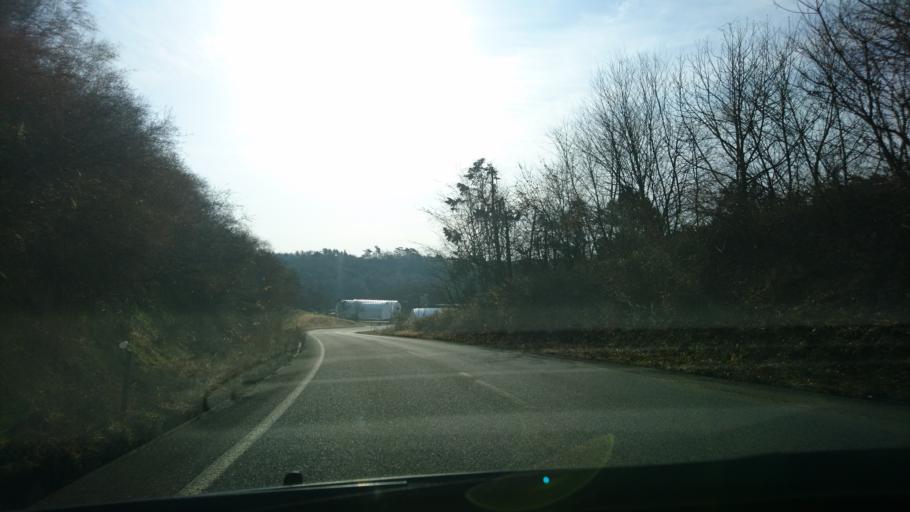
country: JP
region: Iwate
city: Ichinoseki
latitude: 38.8521
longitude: 141.2067
